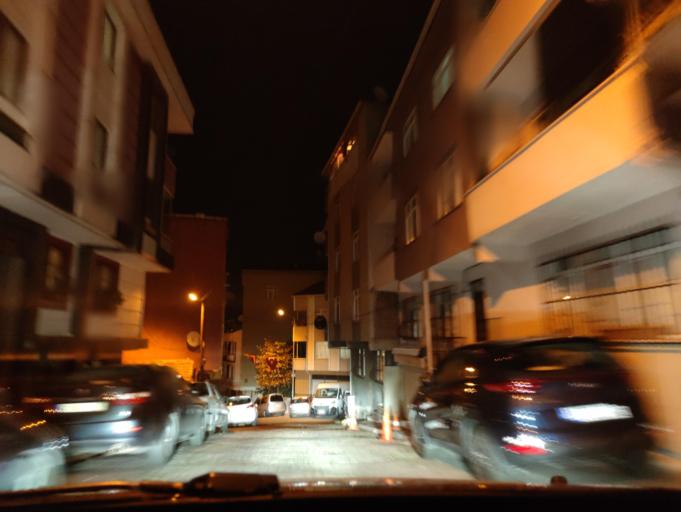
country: TR
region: Istanbul
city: Sisli
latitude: 41.0582
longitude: 28.9603
